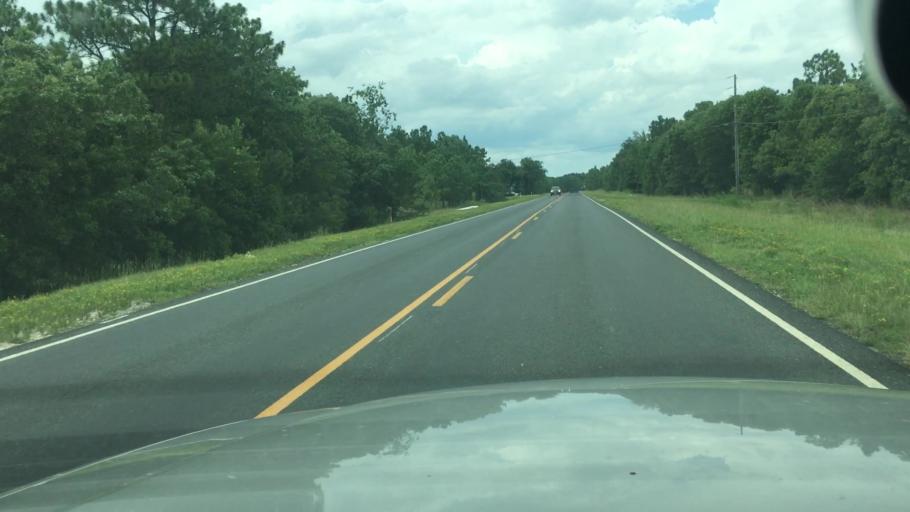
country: US
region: North Carolina
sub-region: Cumberland County
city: Hope Mills
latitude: 34.9693
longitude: -78.8932
